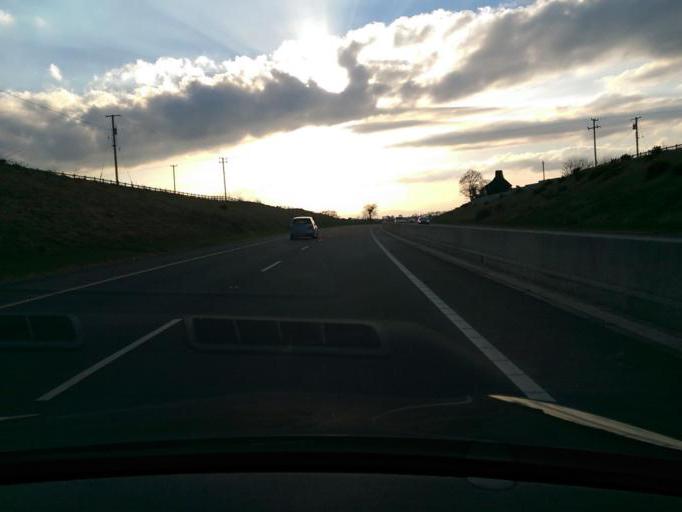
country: IE
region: Munster
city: Nenagh Bridge
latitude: 52.8752
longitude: -8.0208
